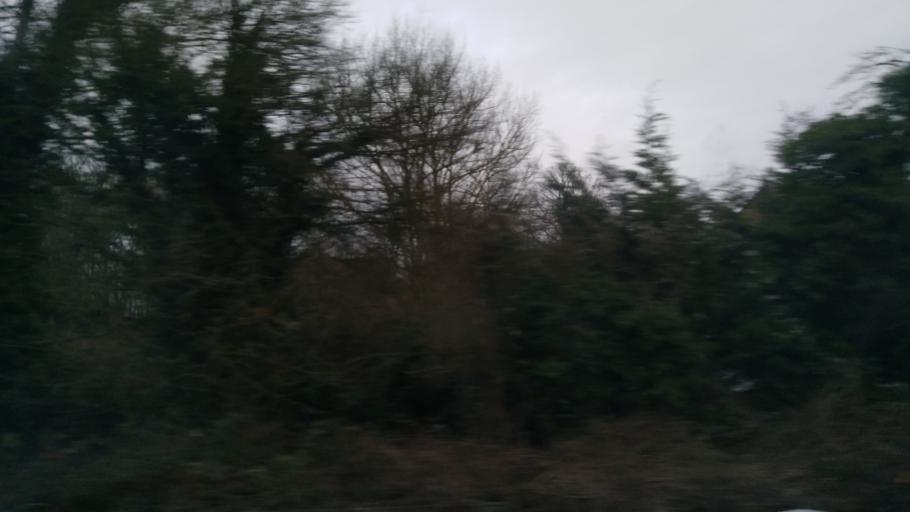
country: GB
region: England
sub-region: Kent
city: Headcorn
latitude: 51.1663
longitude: 0.6189
